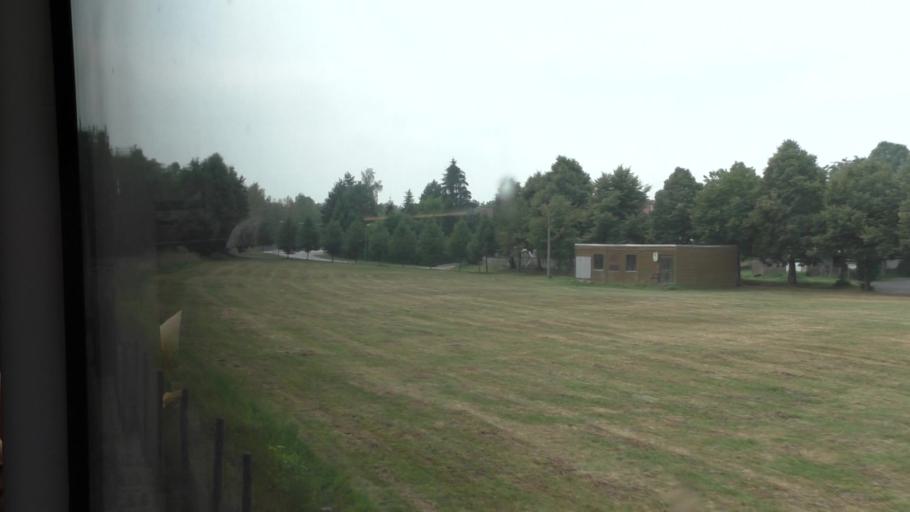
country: DE
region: Saxony
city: Hirschfelde
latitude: 50.9454
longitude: 14.8928
